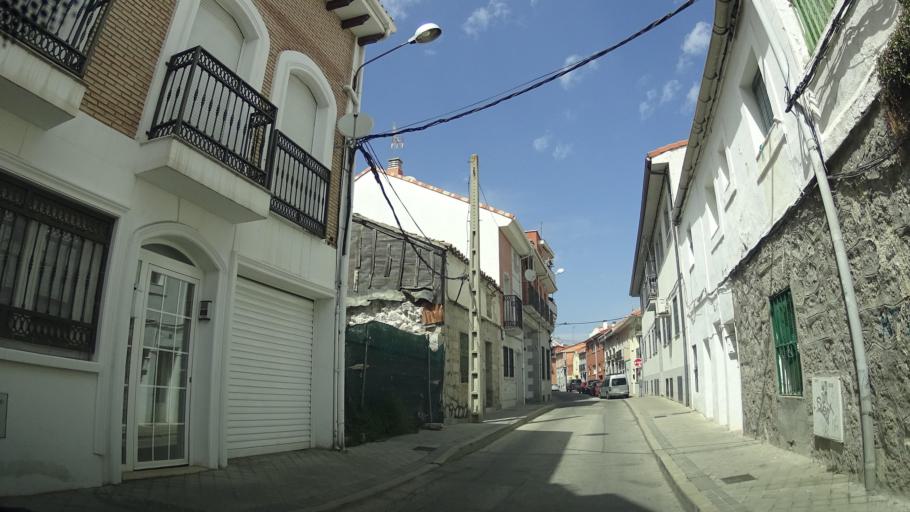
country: ES
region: Madrid
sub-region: Provincia de Madrid
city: Colmenar Viejo
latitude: 40.6621
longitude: -3.7706
